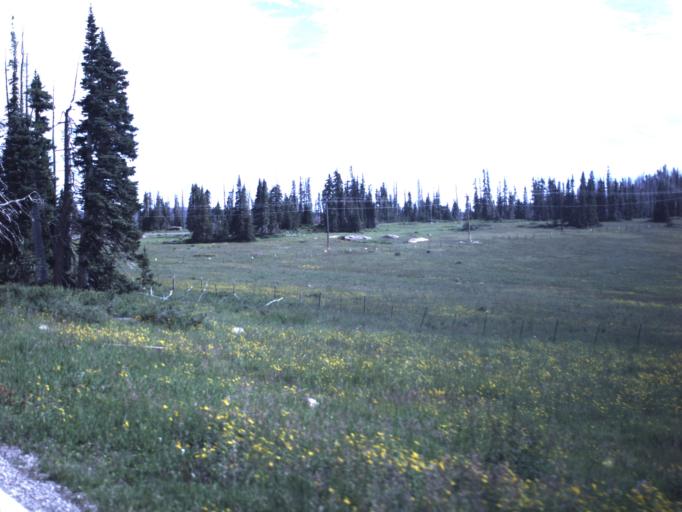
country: US
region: Utah
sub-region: Iron County
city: Cedar City
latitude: 37.6038
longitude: -112.8508
